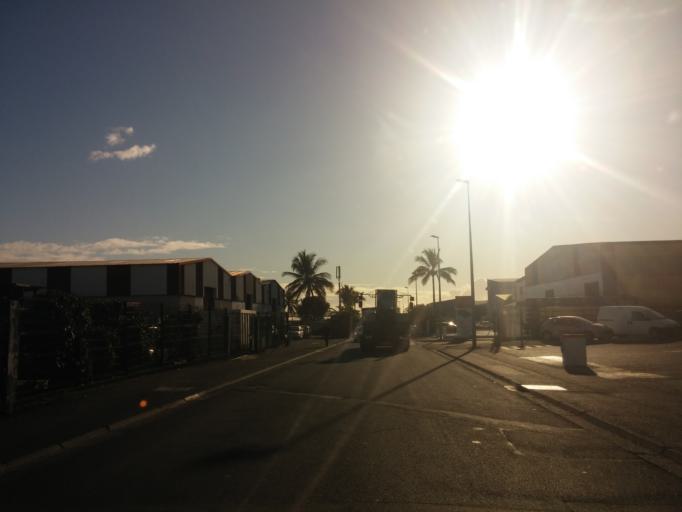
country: RE
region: Reunion
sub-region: Reunion
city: Le Port
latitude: -20.9395
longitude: 55.3137
